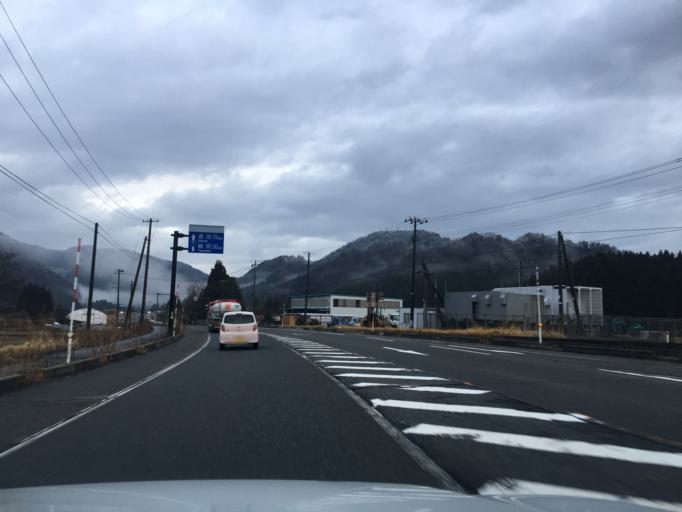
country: JP
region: Niigata
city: Murakami
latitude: 38.4400
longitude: 139.5910
